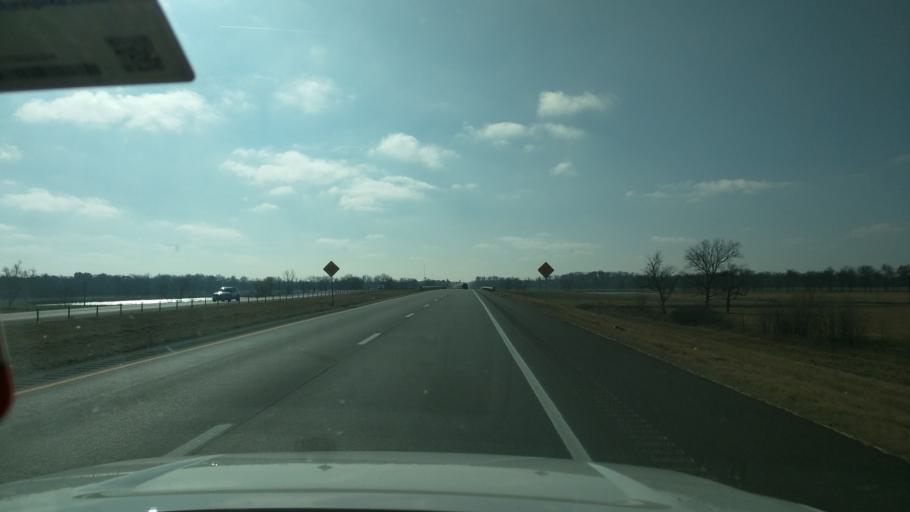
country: US
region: Oklahoma
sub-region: Washington County
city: Bartlesville
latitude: 36.6581
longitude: -95.9356
